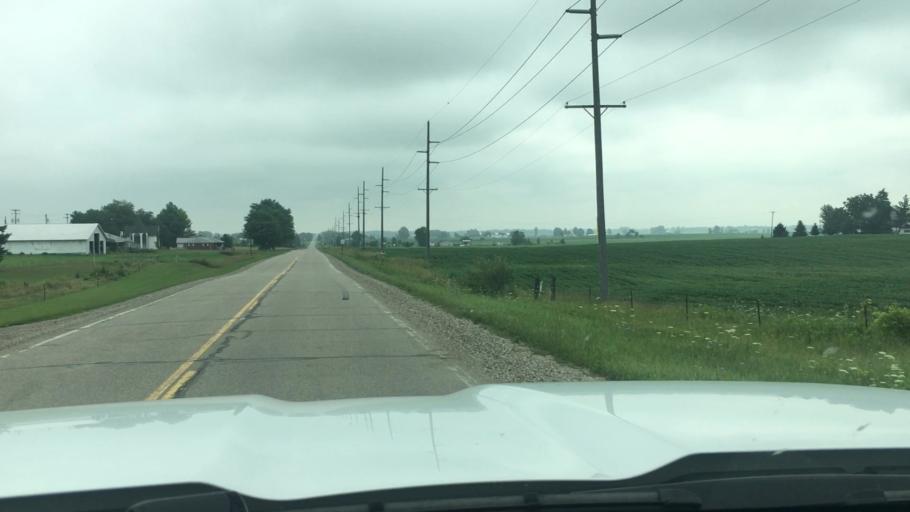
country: US
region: Michigan
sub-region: Sanilac County
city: Brown City
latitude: 43.2559
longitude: -83.0231
